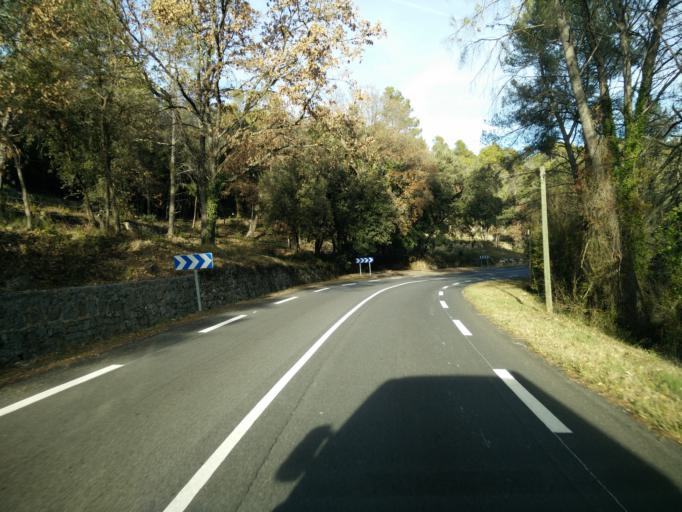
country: FR
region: Provence-Alpes-Cote d'Azur
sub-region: Departement du Var
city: Montauroux
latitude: 43.6084
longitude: 6.8102
